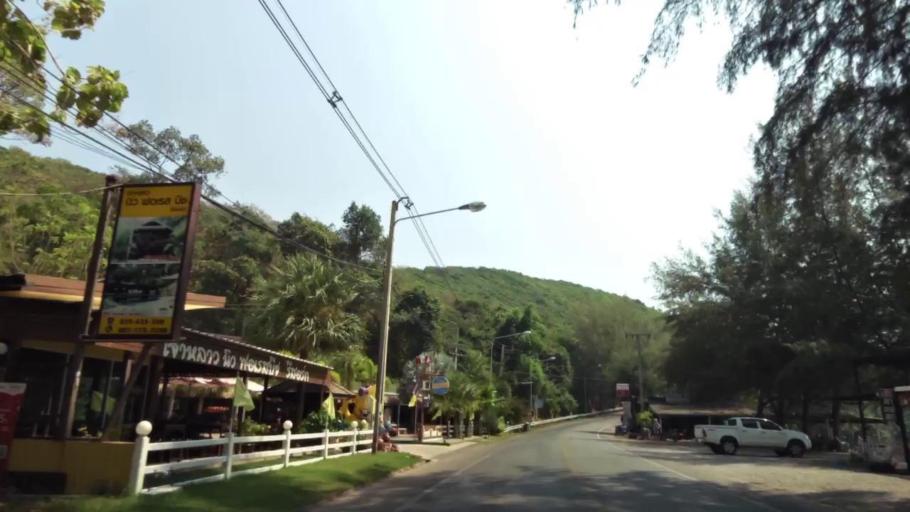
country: TH
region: Chanthaburi
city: Tha Mai
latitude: 12.5323
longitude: 101.9443
